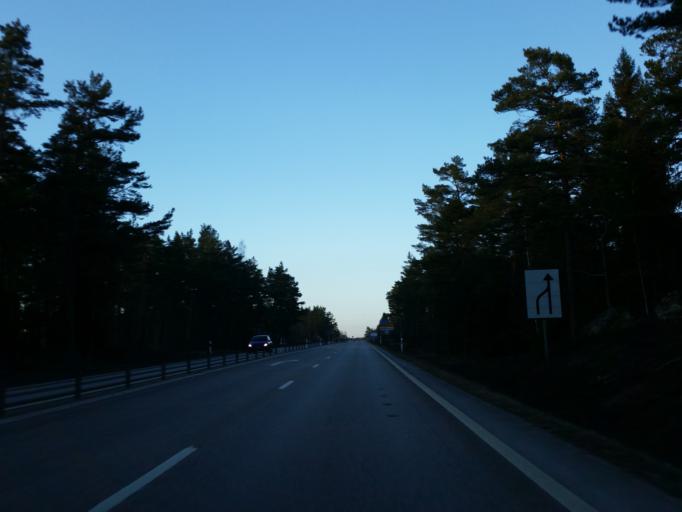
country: SE
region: Kalmar
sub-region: Oskarshamns Kommun
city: Oskarshamn
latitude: 57.3484
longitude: 16.4902
